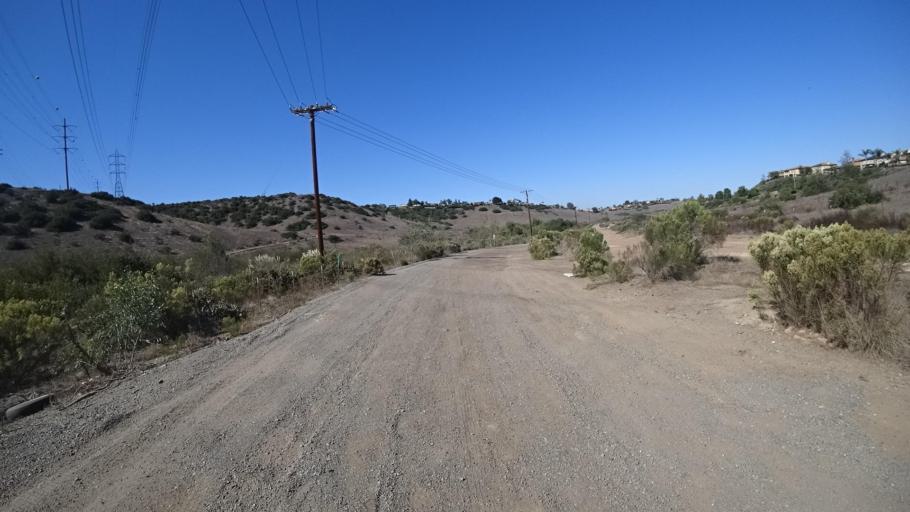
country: US
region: California
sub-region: San Diego County
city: Bonita
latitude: 32.6639
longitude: -116.9893
